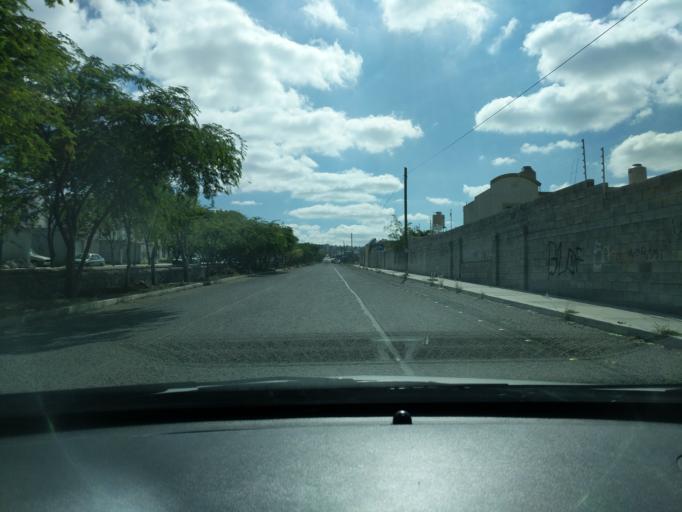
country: MX
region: Queretaro
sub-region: Queretaro
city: Patria Nueva
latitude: 20.6389
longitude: -100.4878
